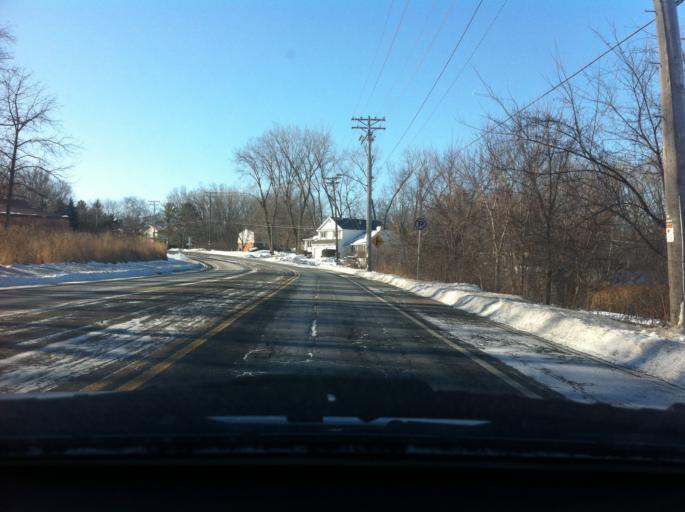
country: US
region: Wisconsin
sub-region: Dane County
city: Middleton
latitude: 43.0895
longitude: -89.5014
